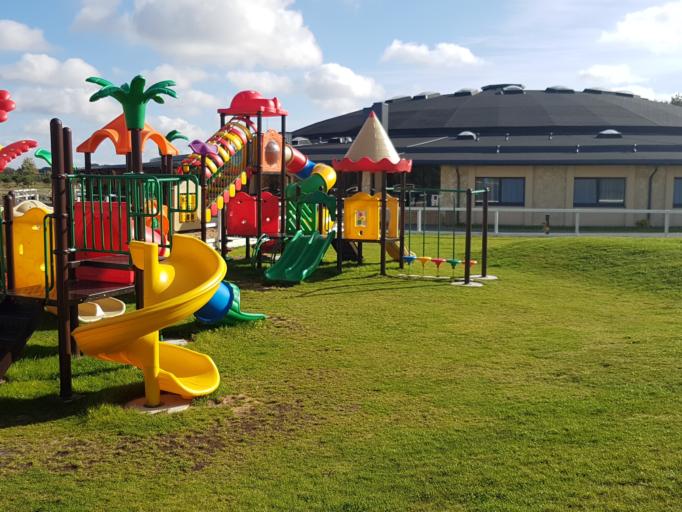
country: LT
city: Moletai
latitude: 55.0405
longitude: 25.4122
